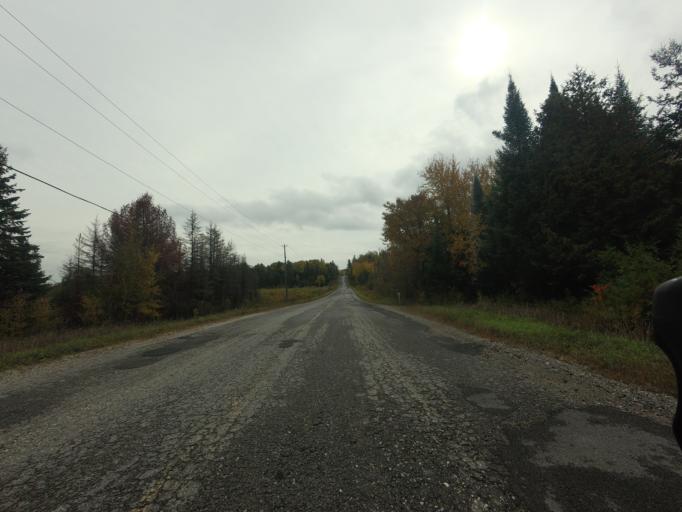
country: CA
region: Ontario
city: Perth
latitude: 45.1197
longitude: -76.5178
